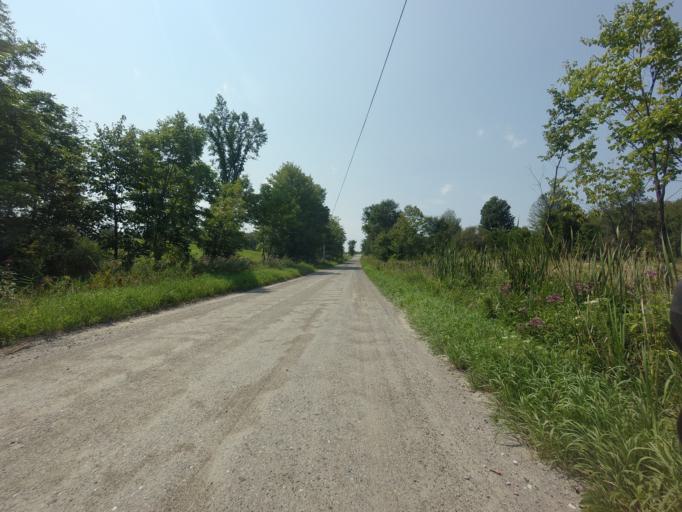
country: CA
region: Ontario
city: Kingston
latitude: 44.6411
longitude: -76.6636
